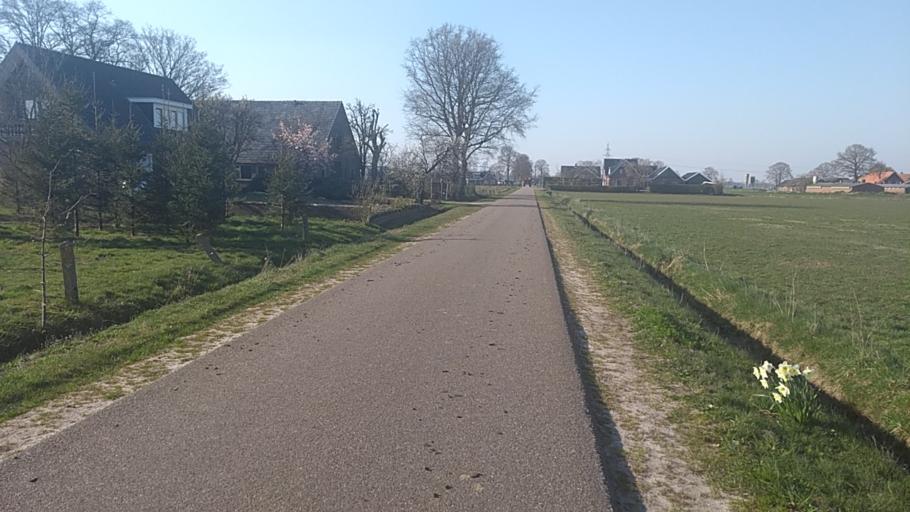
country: NL
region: Overijssel
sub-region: Gemeente Almelo
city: Almelo
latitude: 52.3892
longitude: 6.7032
